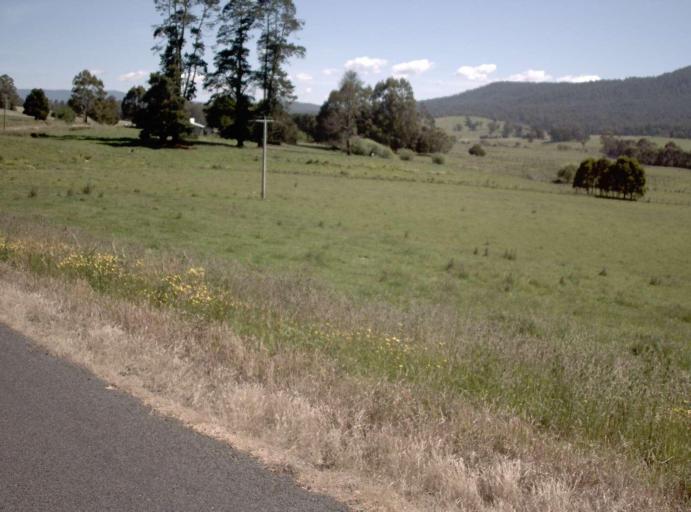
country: AU
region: New South Wales
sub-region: Bombala
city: Bombala
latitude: -37.1992
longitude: 148.7266
